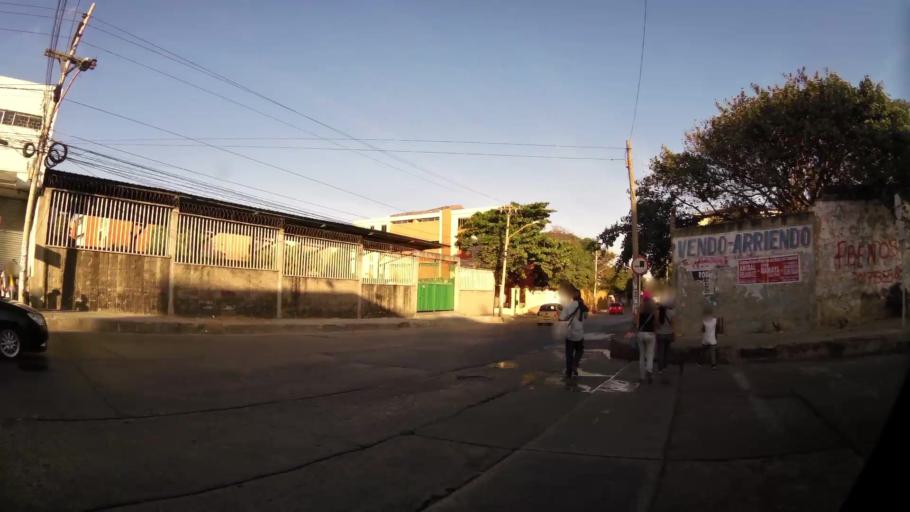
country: CO
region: Atlantico
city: Barranquilla
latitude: 10.9856
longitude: -74.7902
